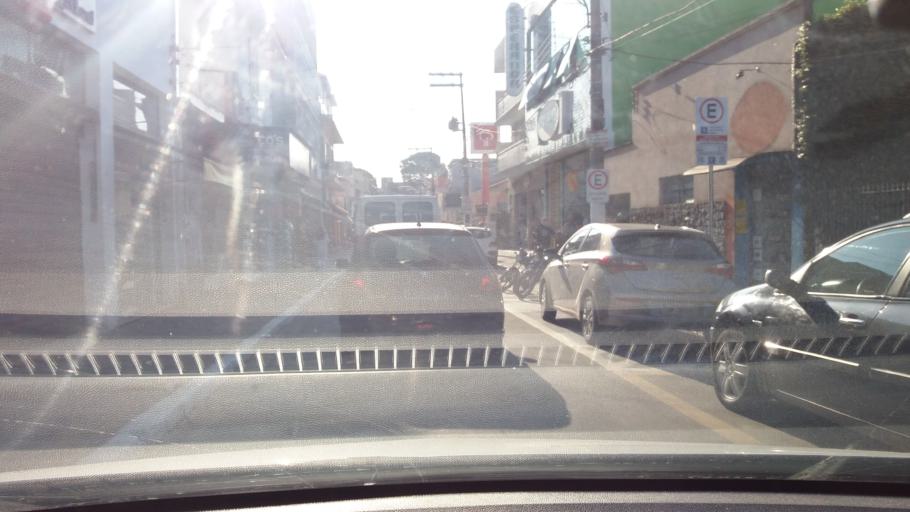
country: BR
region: Sao Paulo
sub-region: Mairipora
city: Mairipora
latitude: -23.3190
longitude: -46.5846
